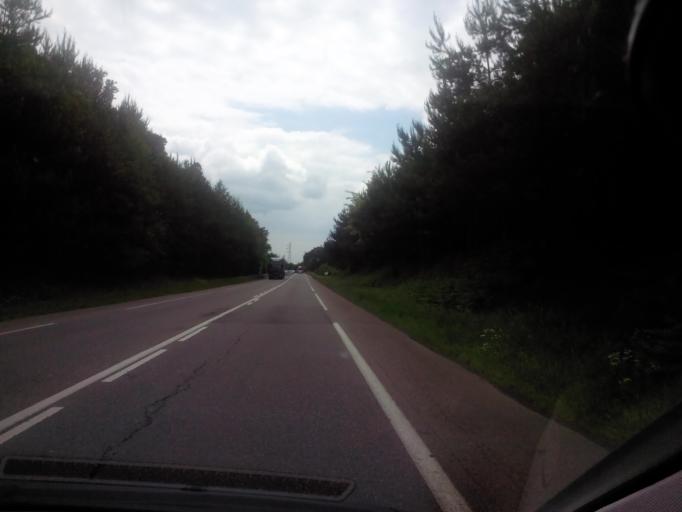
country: FR
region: Lorraine
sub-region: Departement de la Moselle
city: Carling
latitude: 49.1747
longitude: 6.7107
